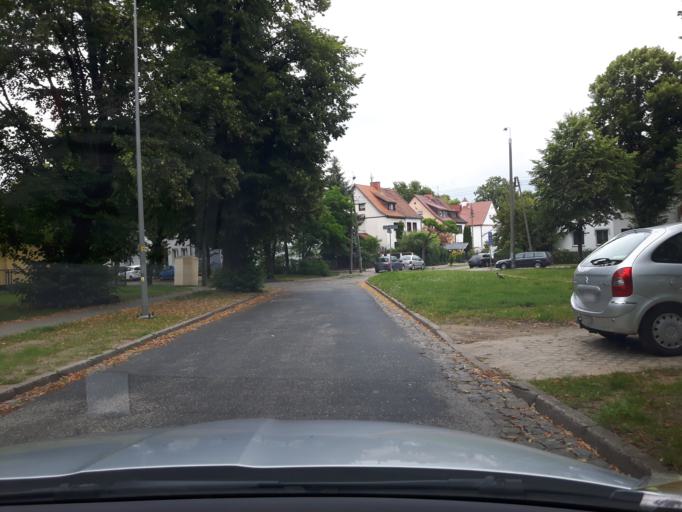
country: PL
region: Pomeranian Voivodeship
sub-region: Sopot
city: Sopot
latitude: 54.4103
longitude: 18.5769
